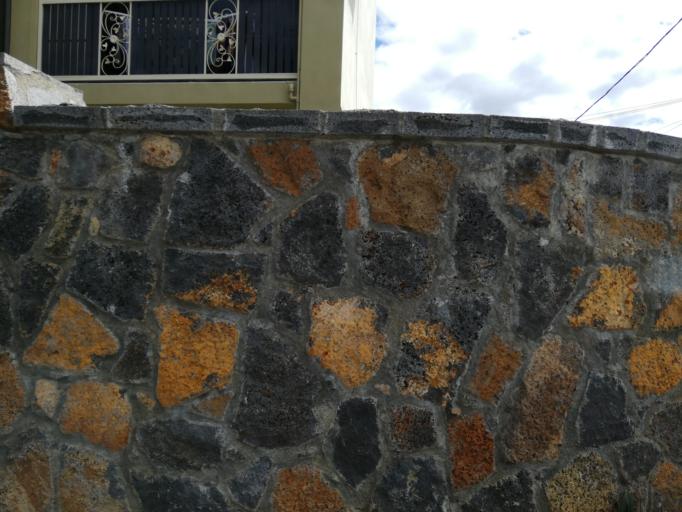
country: MU
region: Moka
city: Moka
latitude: -20.2130
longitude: 57.4711
